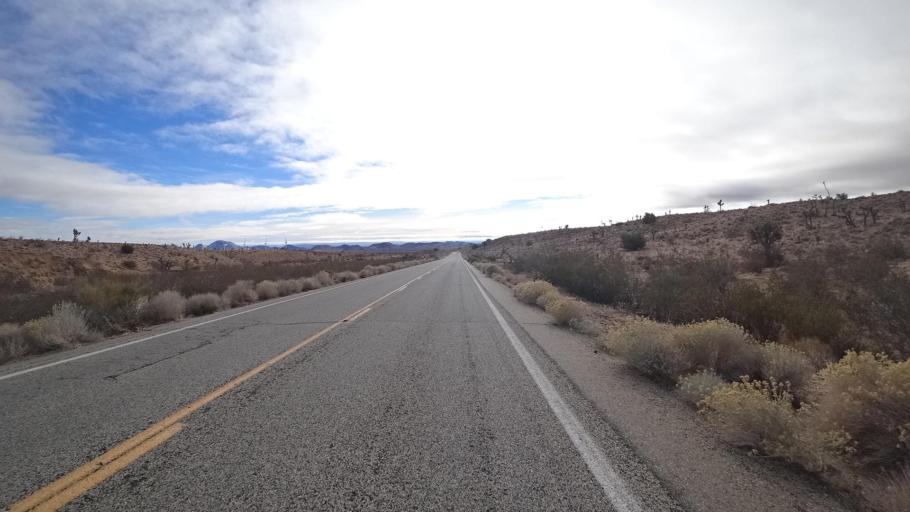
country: US
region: California
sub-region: Kern County
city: Tehachapi
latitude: 35.0031
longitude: -118.3376
